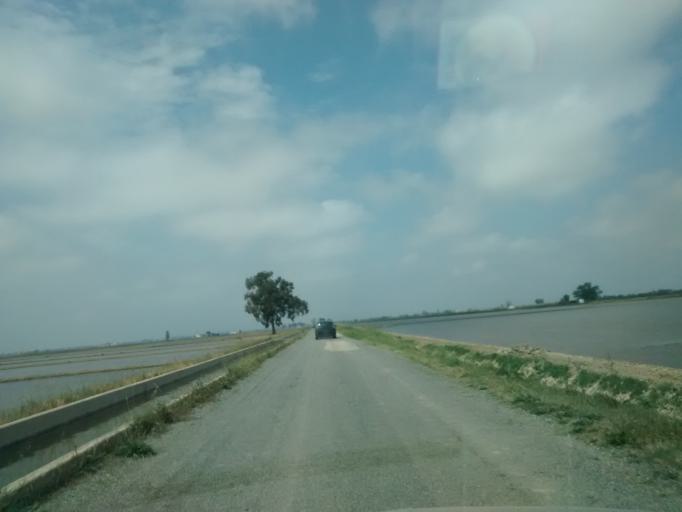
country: ES
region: Catalonia
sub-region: Provincia de Tarragona
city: Deltebre
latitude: 40.6855
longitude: 0.7869
